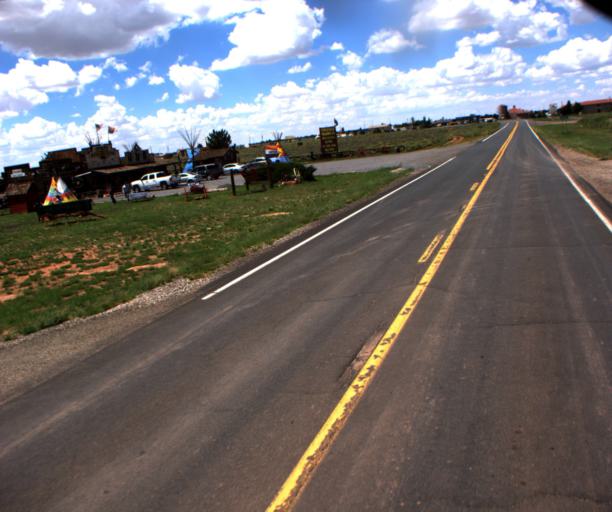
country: US
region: Arizona
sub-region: Coconino County
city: Grand Canyon Village
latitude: 35.6496
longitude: -112.1355
